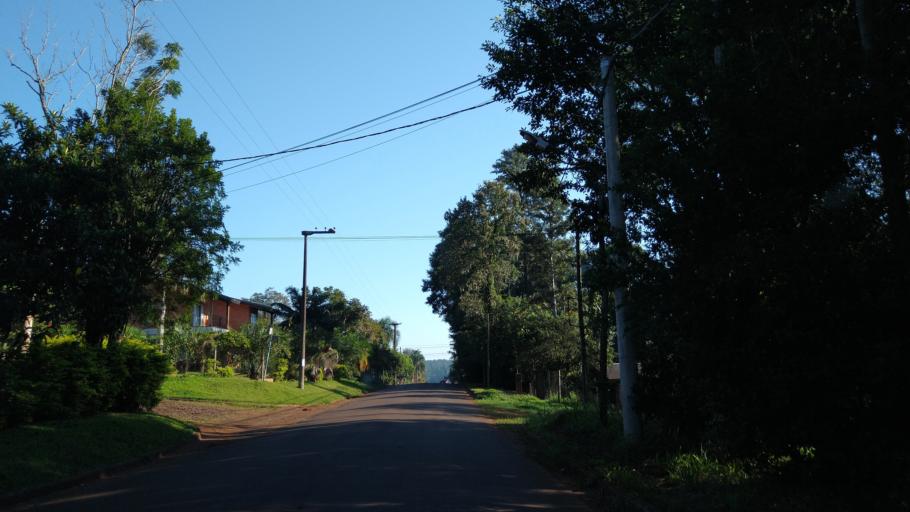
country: AR
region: Misiones
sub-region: Departamento de Montecarlo
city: Montecarlo
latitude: -26.5696
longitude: -54.7457
